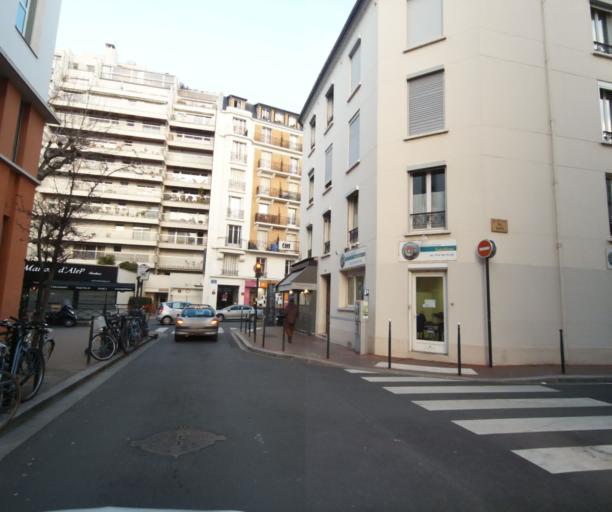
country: FR
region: Ile-de-France
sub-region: Departement des Hauts-de-Seine
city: Asnieres-sur-Seine
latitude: 48.9082
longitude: 2.2848
